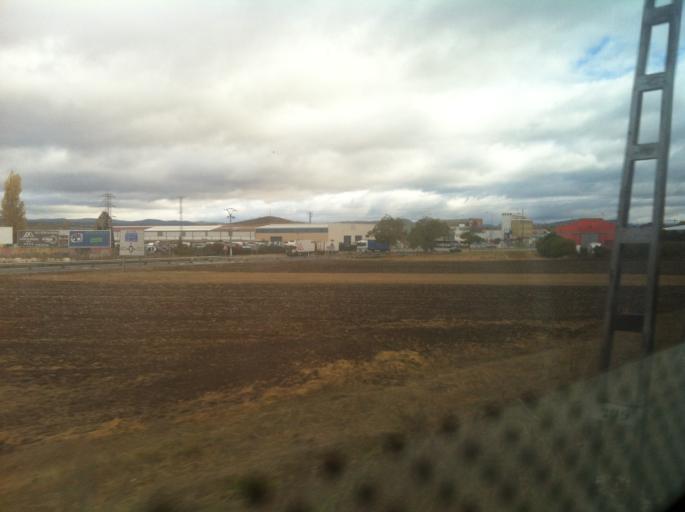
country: ES
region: Castille and Leon
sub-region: Provincia de Burgos
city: Miranda de Ebro
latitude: 42.6846
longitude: -2.9673
